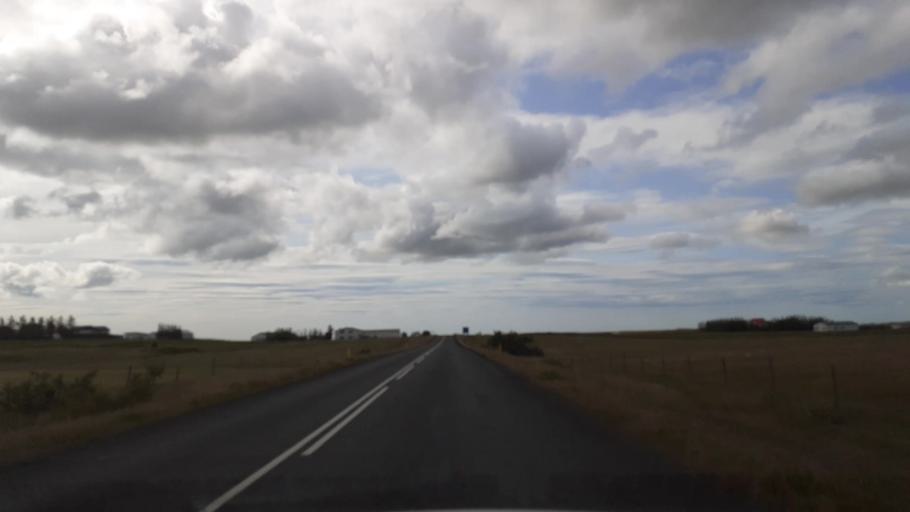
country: IS
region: South
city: Vestmannaeyjar
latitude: 63.8396
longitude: -20.4110
